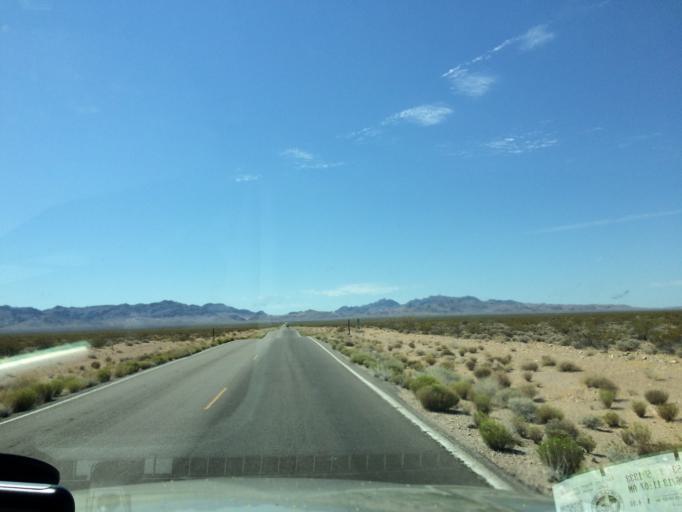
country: US
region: Nevada
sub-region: Clark County
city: Moapa Town
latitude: 36.4766
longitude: -114.7441
